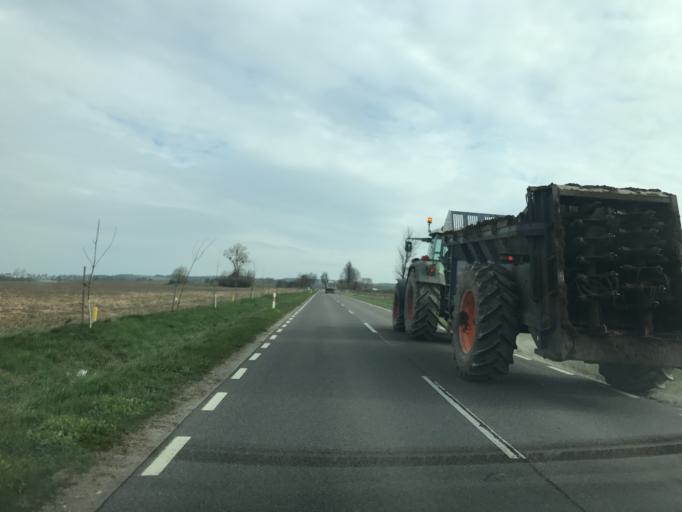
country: PL
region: Warmian-Masurian Voivodeship
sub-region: Powiat ostrodzki
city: Gierzwald
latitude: 53.5150
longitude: 20.0874
